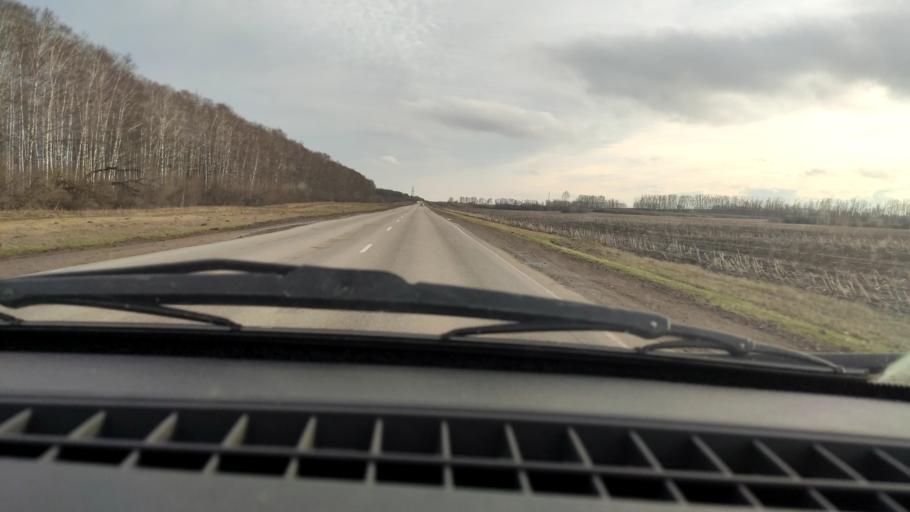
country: RU
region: Bashkortostan
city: Chishmy
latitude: 54.4921
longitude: 55.2759
